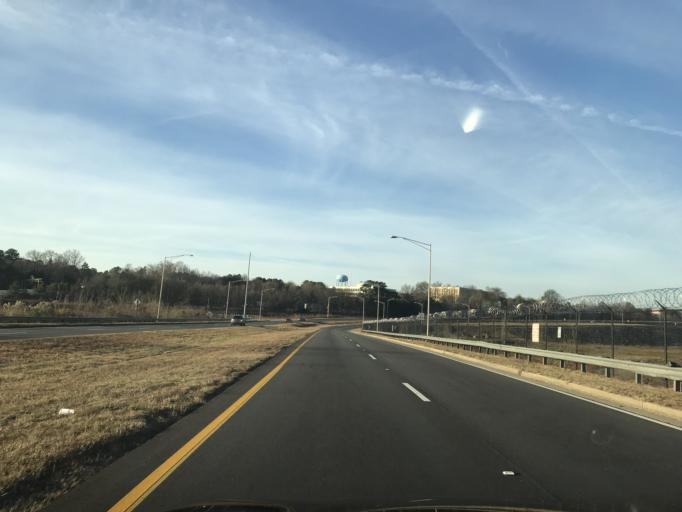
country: US
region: Georgia
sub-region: Fulton County
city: College Park
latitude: 33.6189
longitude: -84.4419
